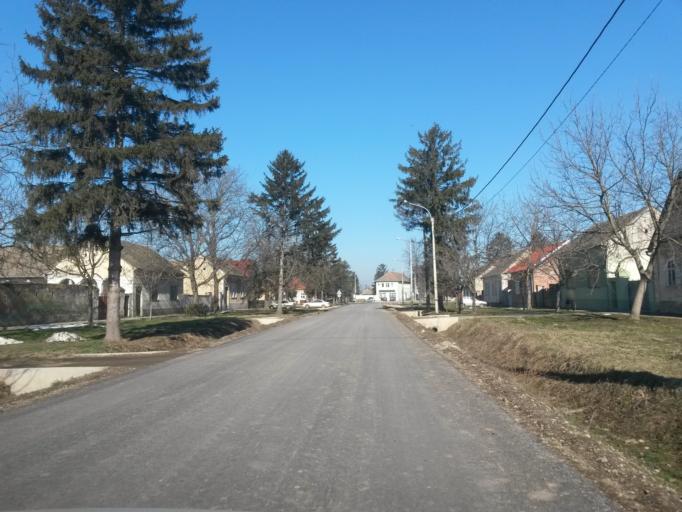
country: HR
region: Vukovarsko-Srijemska
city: Negoslavci
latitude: 45.2766
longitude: 18.9975
